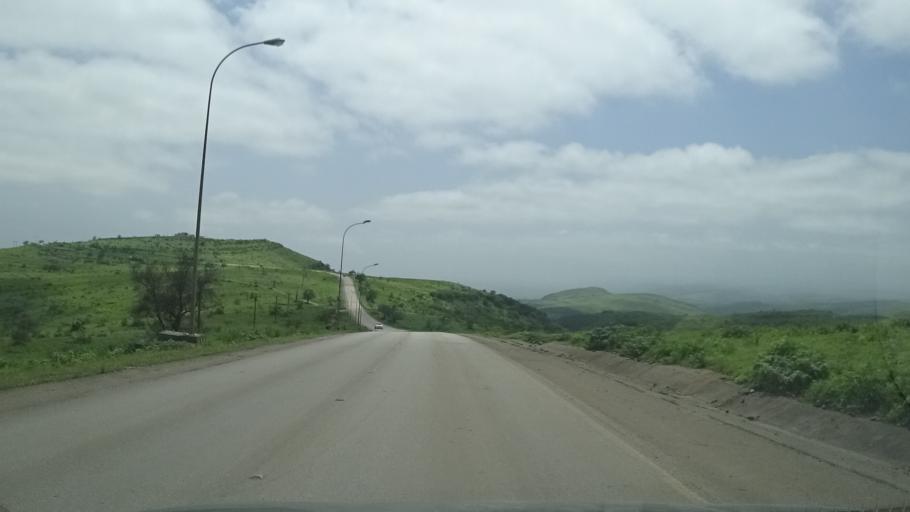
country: OM
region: Zufar
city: Salalah
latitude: 17.1688
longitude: 54.2253
